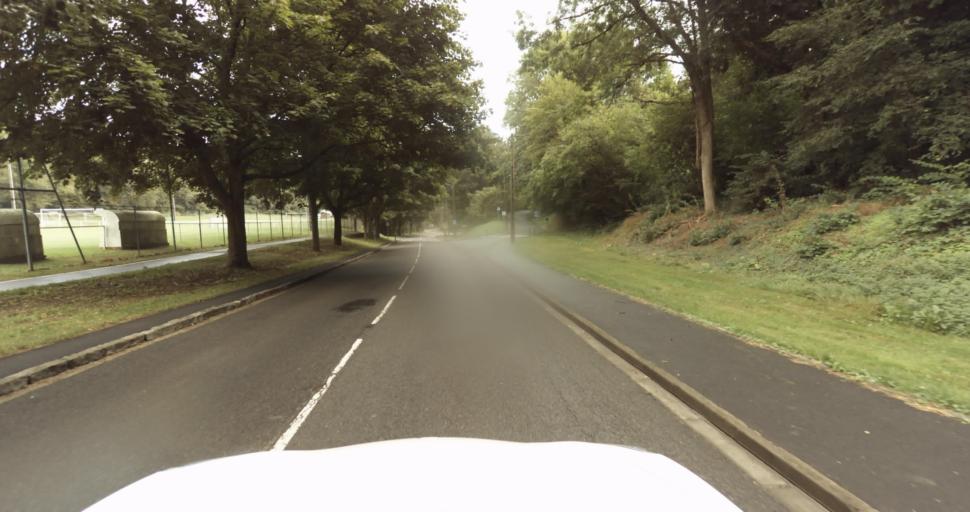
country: FR
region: Haute-Normandie
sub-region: Departement de l'Eure
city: Evreux
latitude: 49.0333
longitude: 1.1462
